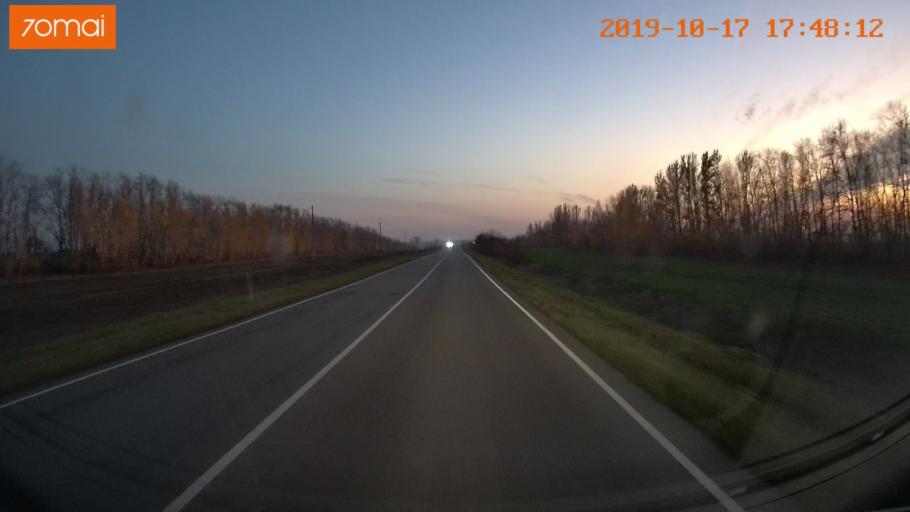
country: RU
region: Tula
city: Yepifan'
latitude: 53.6959
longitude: 38.6960
